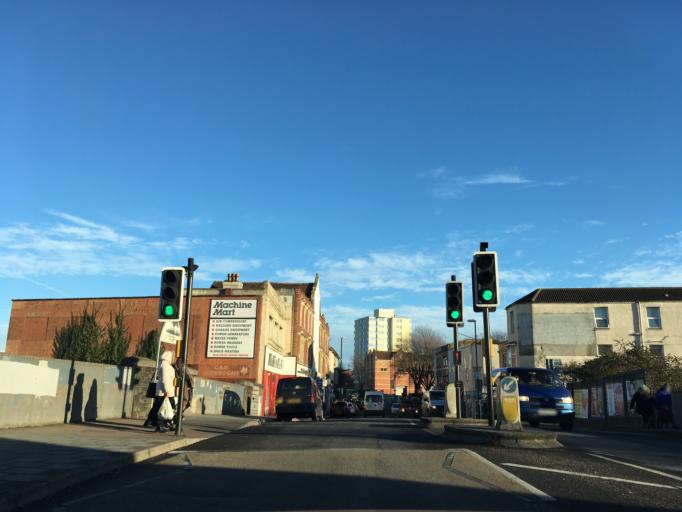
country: GB
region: England
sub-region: Bristol
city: Bristol
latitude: 51.4580
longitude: -2.5647
